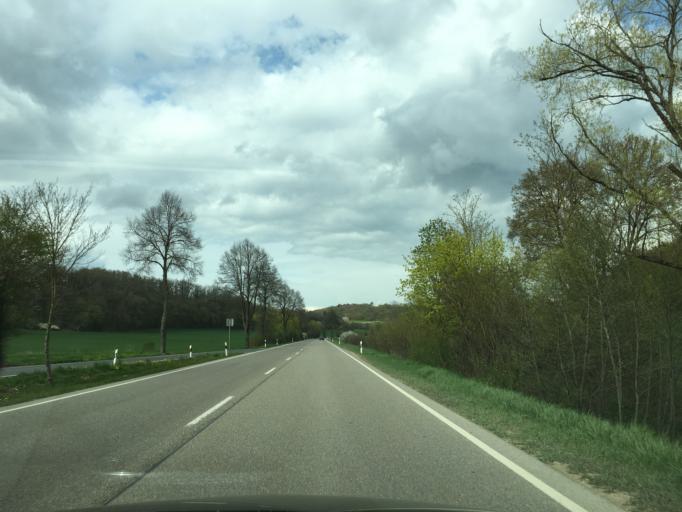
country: DE
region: Bavaria
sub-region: Regierungsbezirk Mittelfranken
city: Treuchtlingen
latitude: 48.9296
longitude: 10.9183
